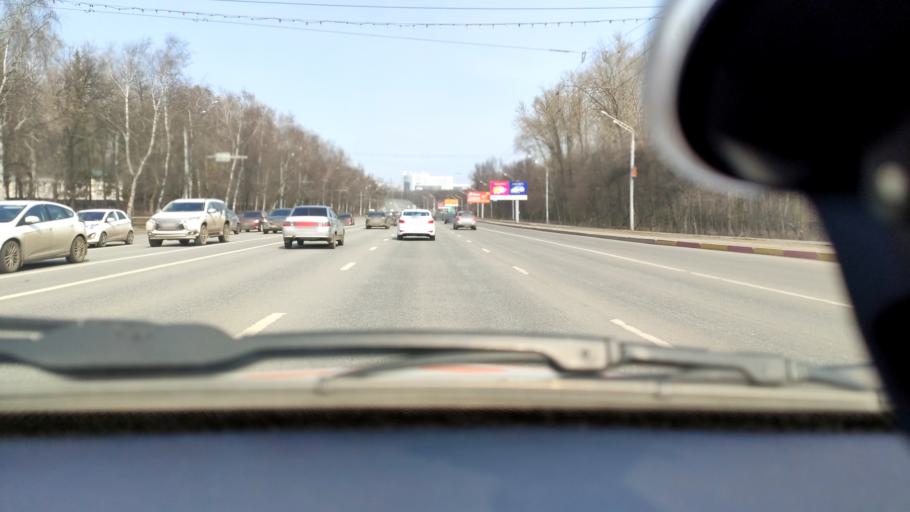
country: RU
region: Bashkortostan
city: Ufa
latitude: 54.8002
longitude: 56.0457
